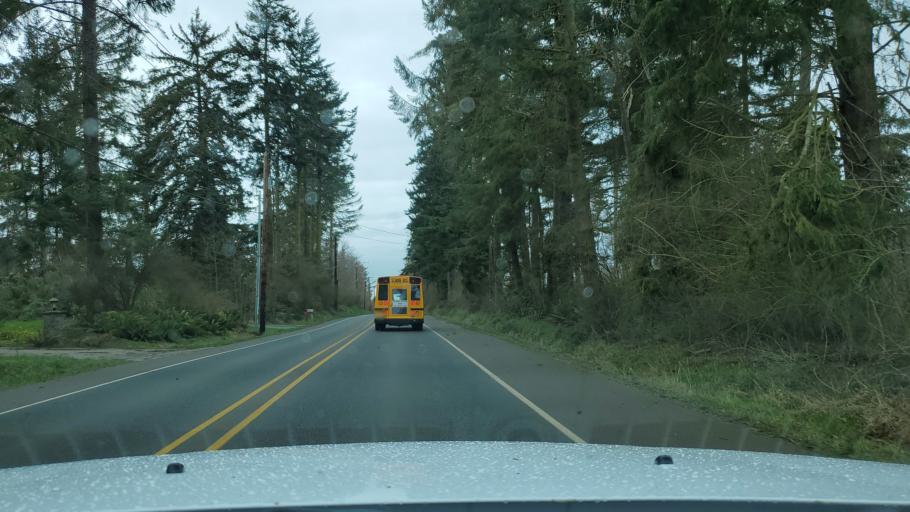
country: US
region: Washington
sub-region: Island County
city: Ault Field
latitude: 48.2919
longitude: -122.7255
